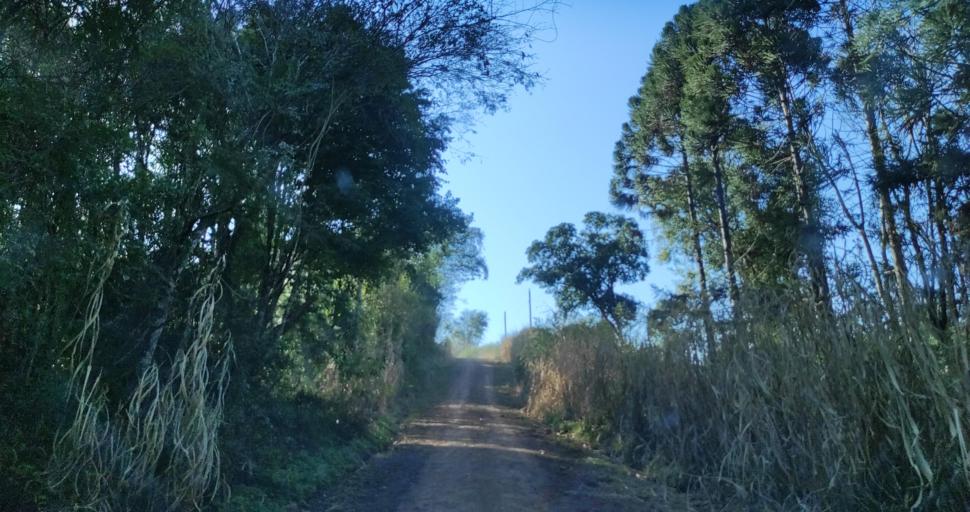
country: AR
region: Misiones
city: Capiovi
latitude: -26.8968
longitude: -55.0930
